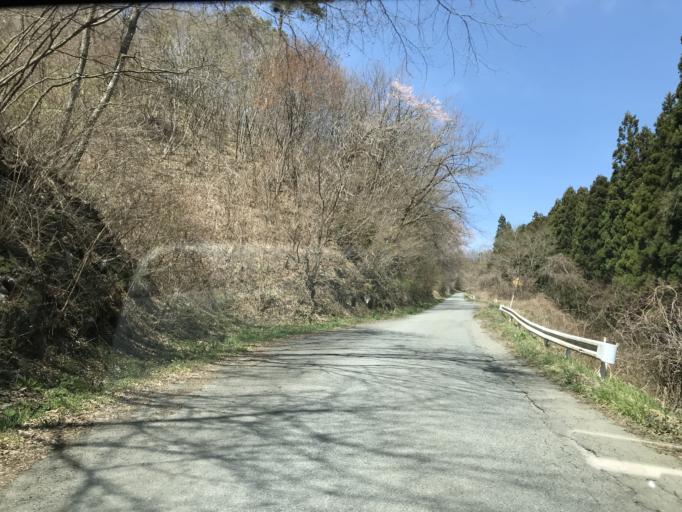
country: JP
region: Iwate
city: Ichinoseki
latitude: 38.8249
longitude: 141.2862
